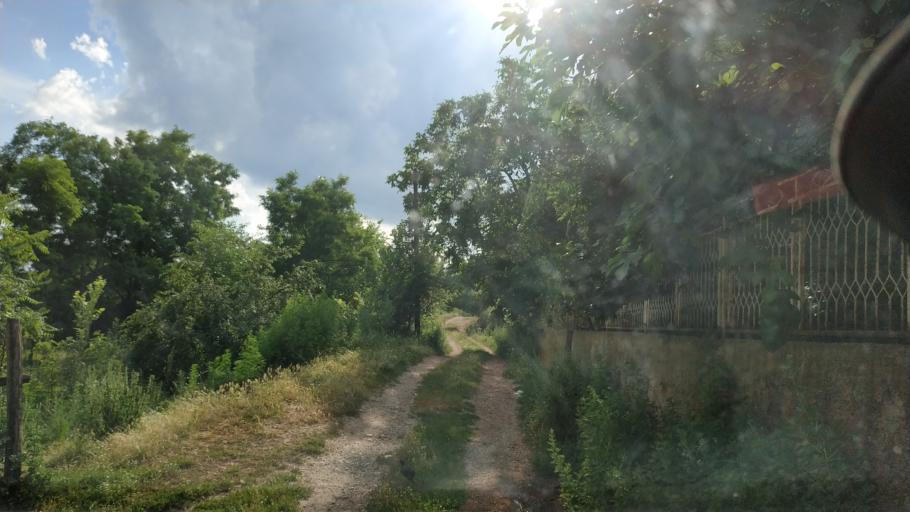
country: RS
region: Central Serbia
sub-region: Nisavski Okrug
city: Aleksinac
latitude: 43.6037
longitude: 21.6977
